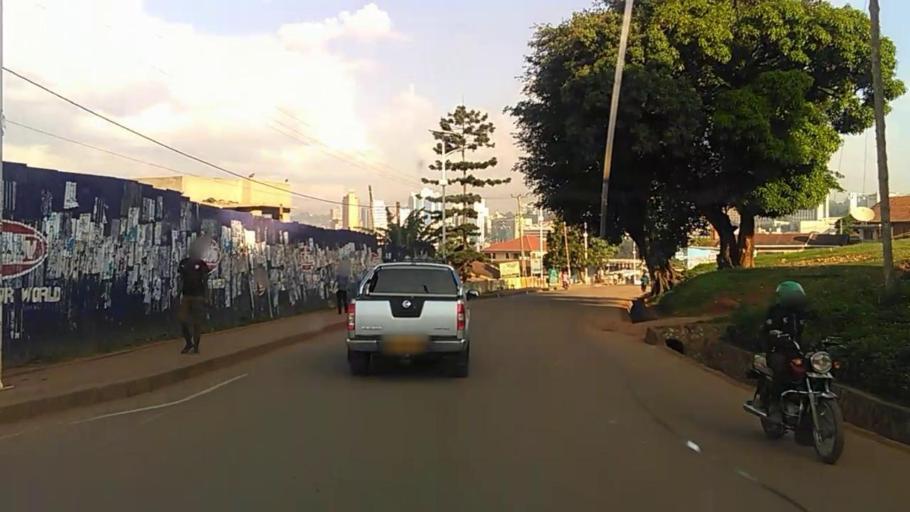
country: UG
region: Central Region
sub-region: Kampala District
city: Kampala
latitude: 0.3087
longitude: 32.5947
